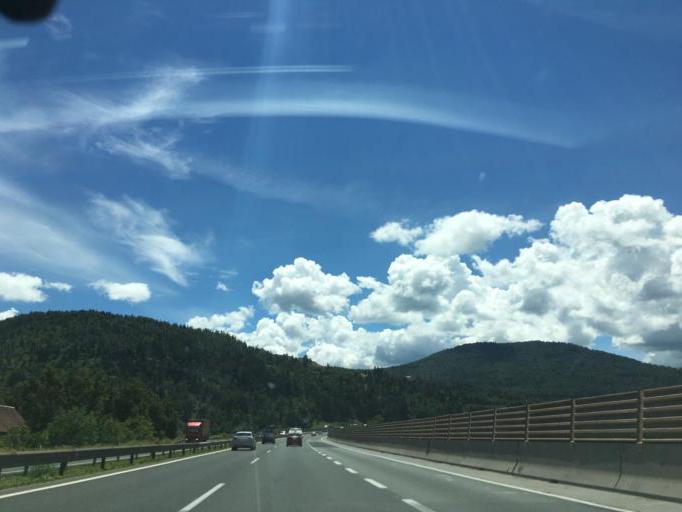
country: SI
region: Vrhnika
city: Verd
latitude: 45.9623
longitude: 14.3051
